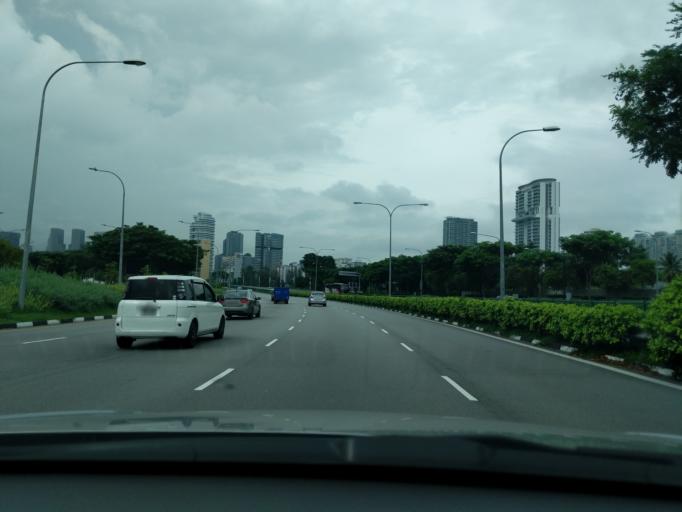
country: SG
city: Singapore
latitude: 1.3066
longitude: 103.8727
